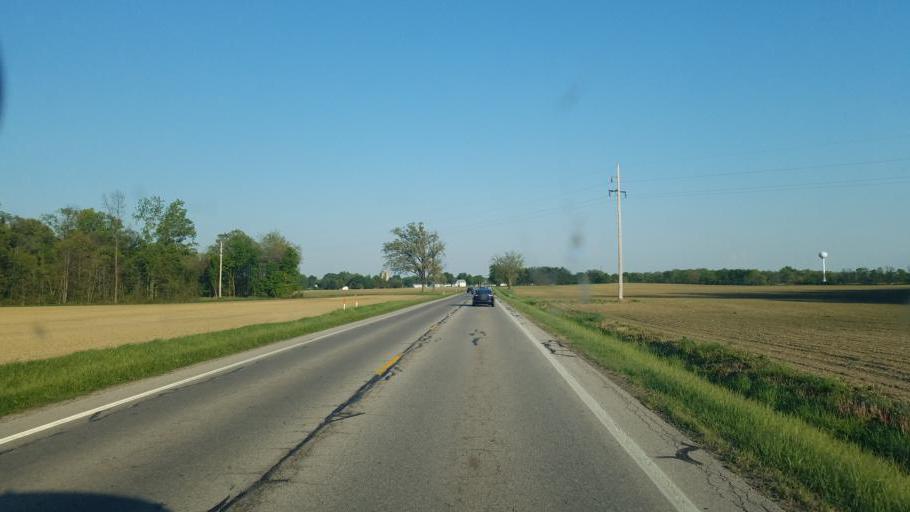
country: US
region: Ohio
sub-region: Morrow County
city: Mount Gilead
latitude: 40.5654
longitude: -82.8787
